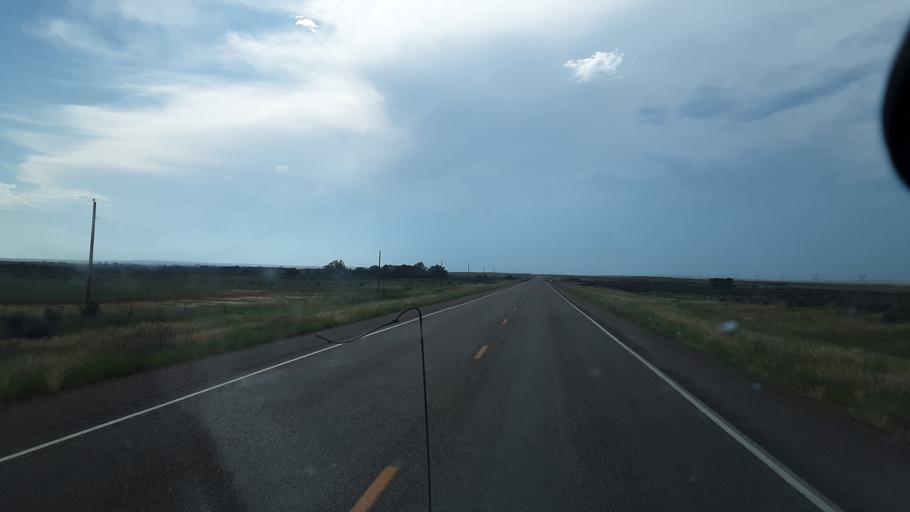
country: US
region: Wyoming
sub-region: Crook County
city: Sundance
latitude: 45.1052
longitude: -104.5873
